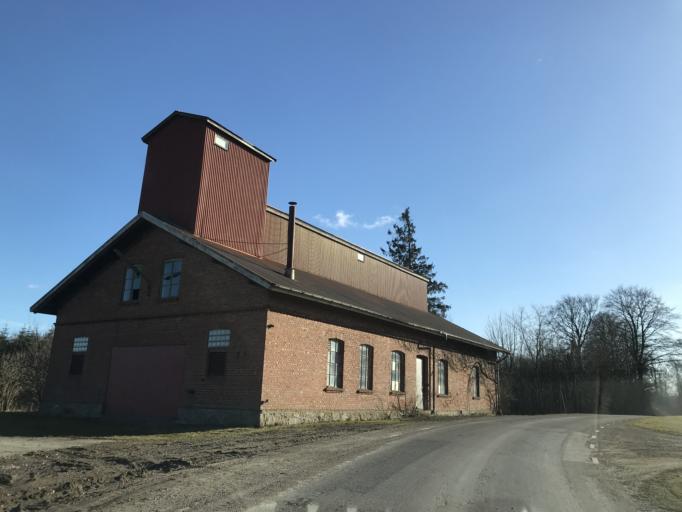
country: SE
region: Skane
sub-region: Ystads Kommun
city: Ystad
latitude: 55.5524
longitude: 13.8079
